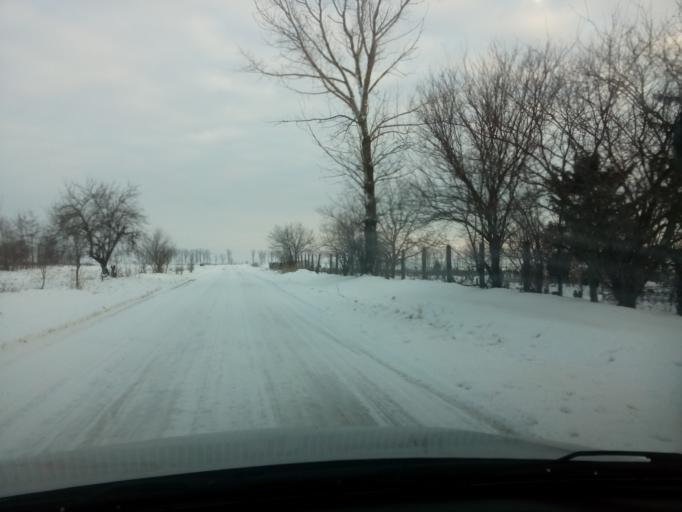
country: RO
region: Calarasi
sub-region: Comuna Luica
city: Luica
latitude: 44.2462
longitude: 26.6119
